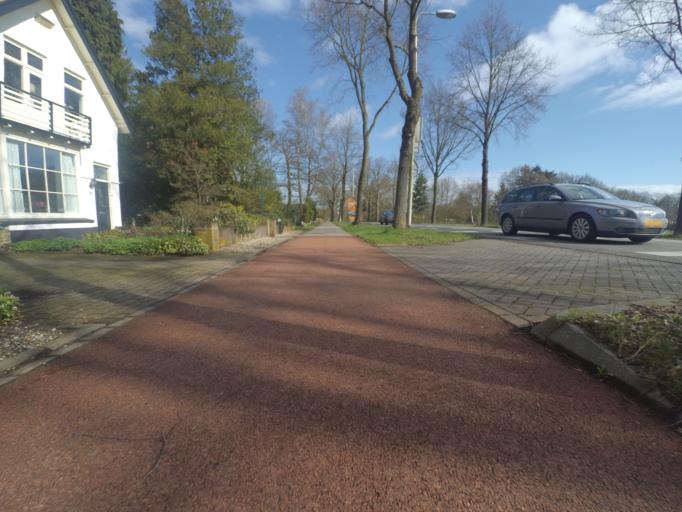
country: NL
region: Gelderland
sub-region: Gemeente Apeldoorn
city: Beekbergen
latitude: 52.1657
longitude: 5.9619
